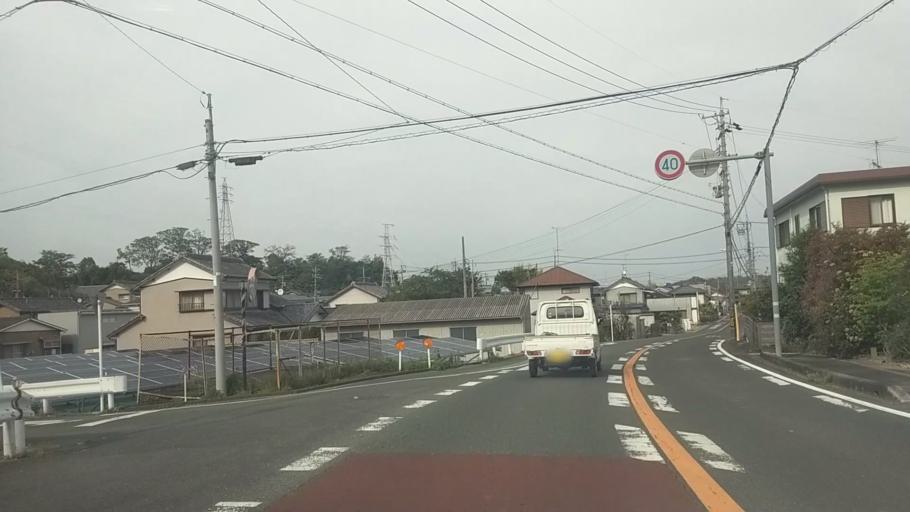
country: JP
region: Shizuoka
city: Kosai-shi
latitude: 34.7378
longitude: 137.6012
